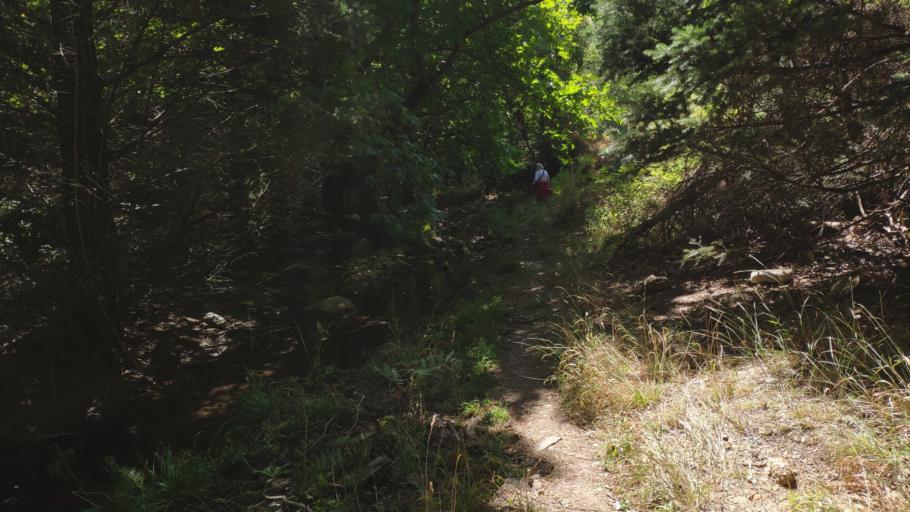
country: GR
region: Peloponnese
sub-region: Nomos Lakonias
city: Kariai
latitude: 37.1745
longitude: 22.5834
